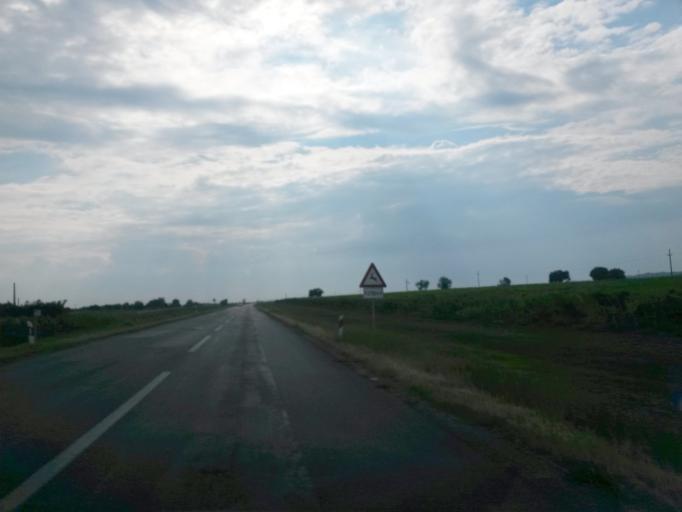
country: HR
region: Osjecko-Baranjska
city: Dalj
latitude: 45.5051
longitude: 19.0174
